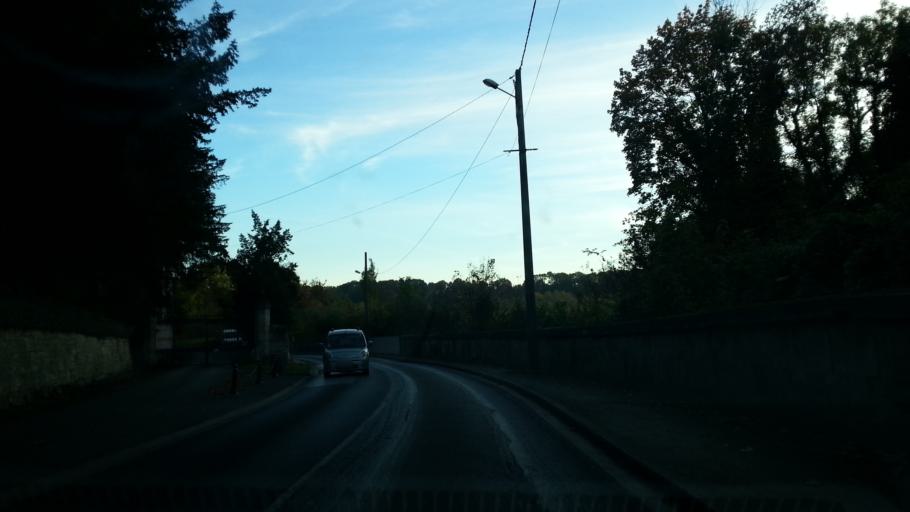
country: FR
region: Picardie
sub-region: Departement de l'Oise
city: Cires-les-Mello
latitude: 49.2700
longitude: 2.3656
